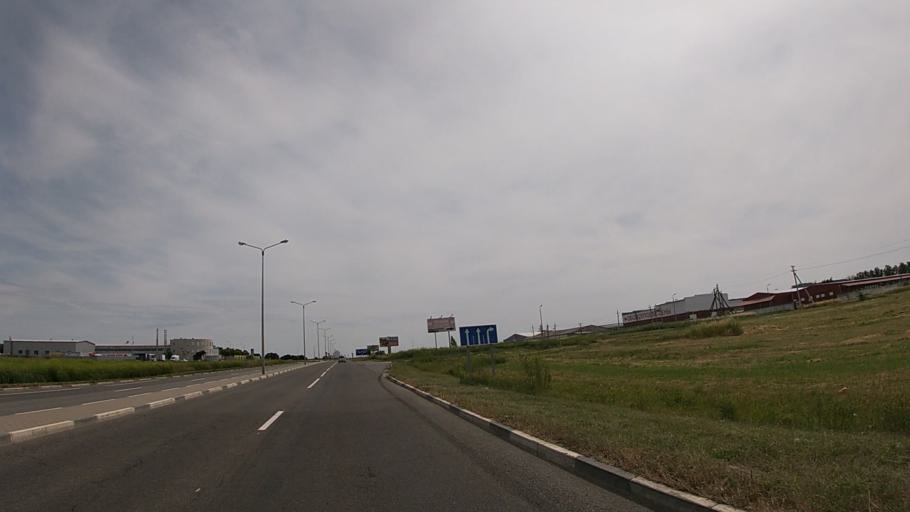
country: RU
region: Belgorod
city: Severnyy
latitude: 50.6600
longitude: 36.5574
